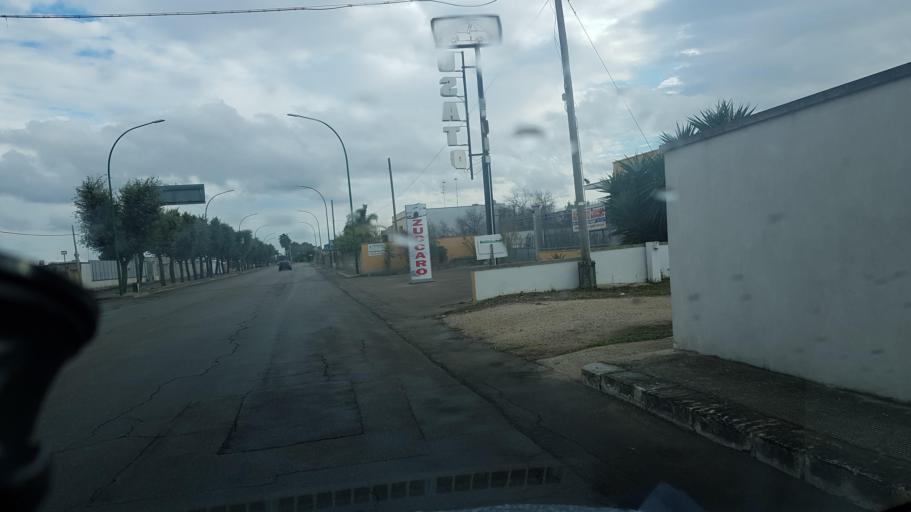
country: IT
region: Apulia
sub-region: Provincia di Lecce
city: Surbo
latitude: 40.3846
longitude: 18.1350
